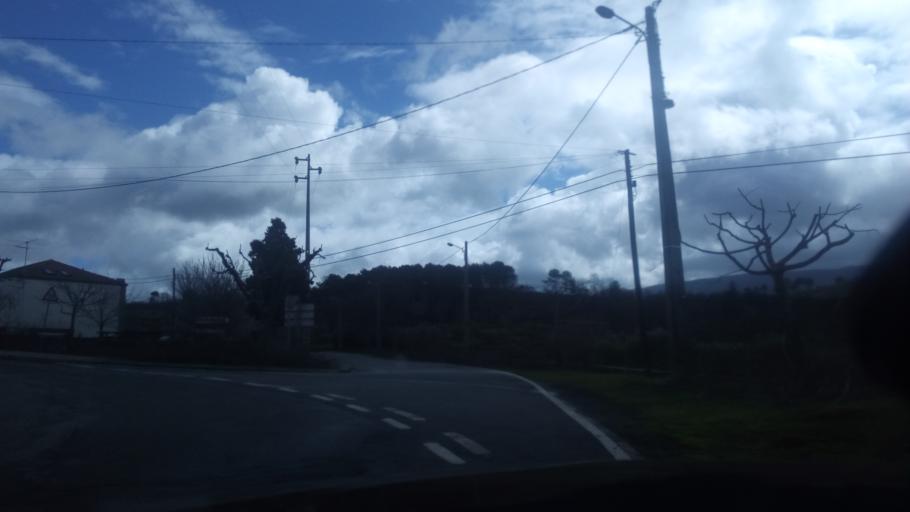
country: PT
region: Guarda
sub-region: Fornos de Algodres
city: Fornos de Algodres
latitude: 40.5869
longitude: -7.4876
